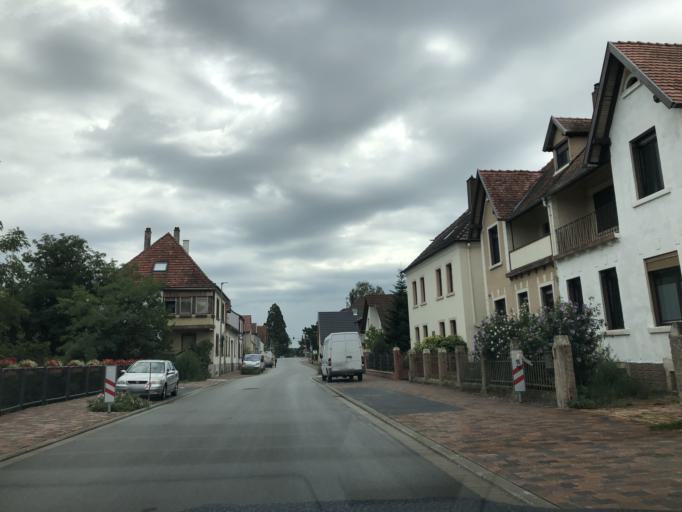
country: DE
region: Rheinland-Pfalz
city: Bellheim
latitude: 49.1903
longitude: 8.2921
